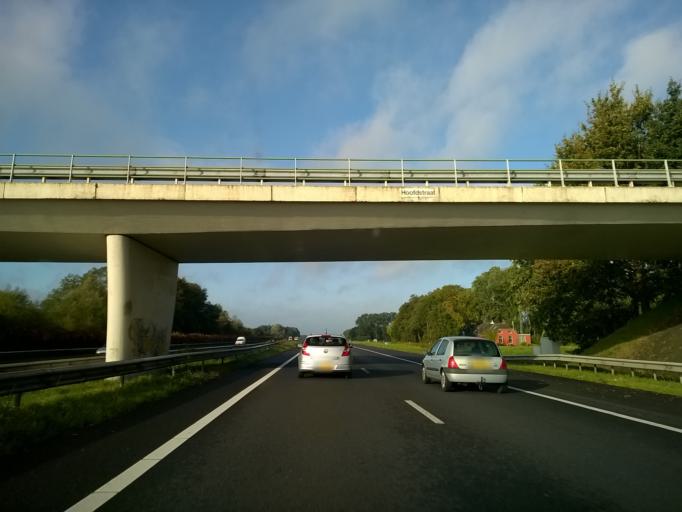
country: NL
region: Groningen
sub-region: Gemeente Zuidhorn
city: Zuidhorn
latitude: 53.1949
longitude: 6.4247
